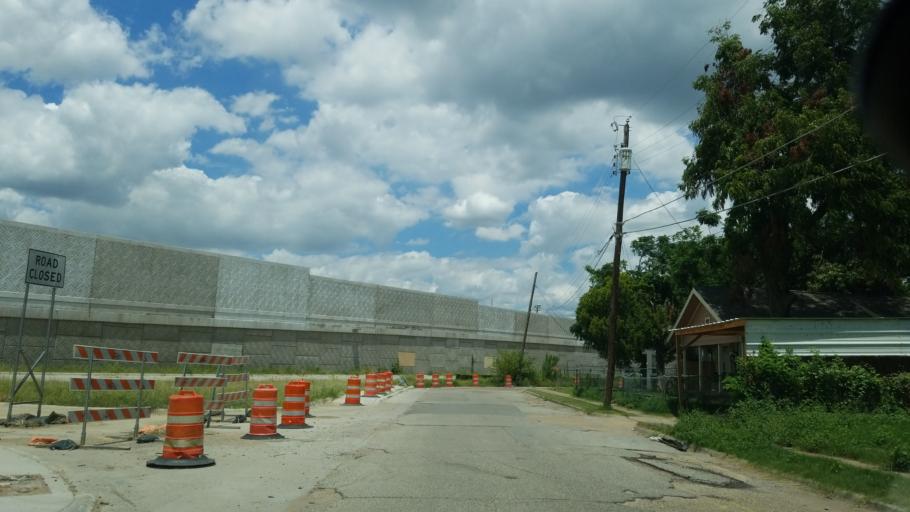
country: US
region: Texas
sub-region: Dallas County
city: Dallas
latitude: 32.7463
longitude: -96.7551
